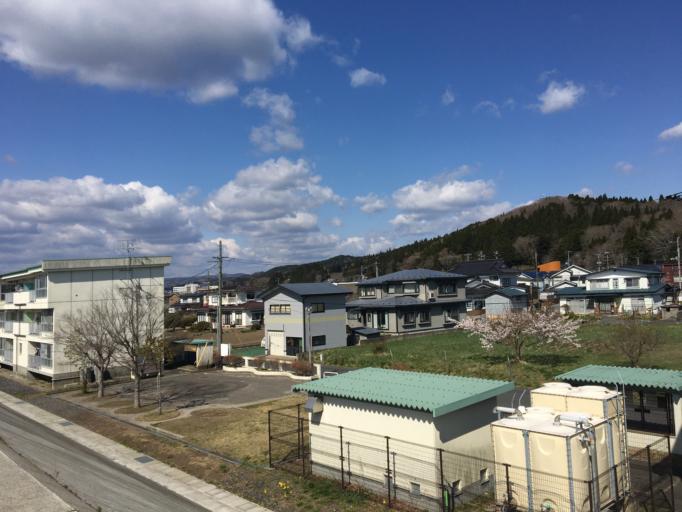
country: JP
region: Aomori
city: Hachinohe
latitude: 40.2005
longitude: 141.7932
